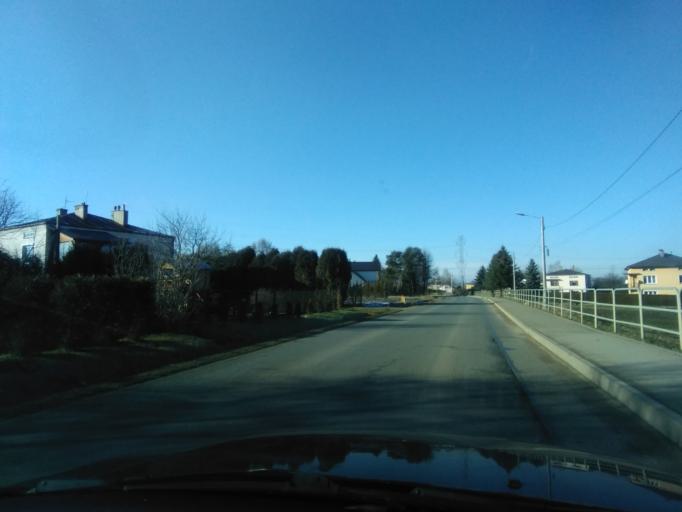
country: PL
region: Subcarpathian Voivodeship
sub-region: Powiat brzozowski
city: Haczow
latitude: 49.6760
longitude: 21.8809
